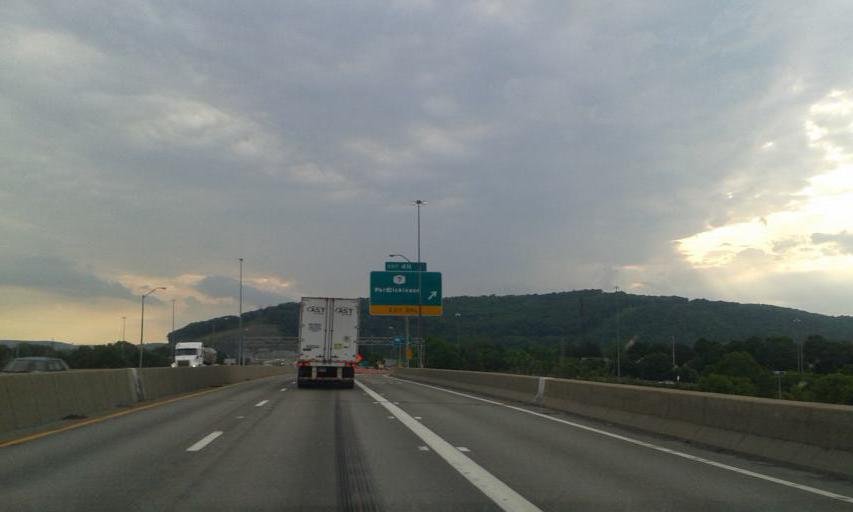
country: US
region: New York
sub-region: Broome County
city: Port Dickinson
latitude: 42.1153
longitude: -75.8917
